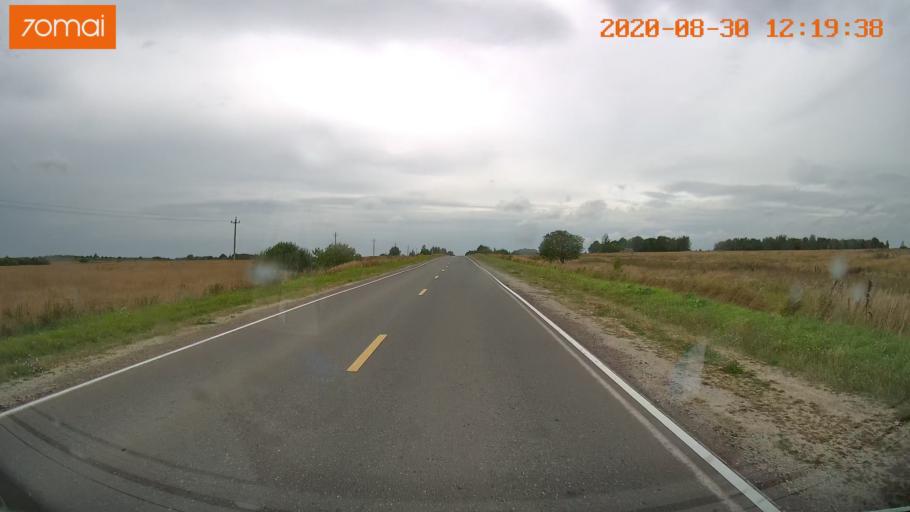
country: RU
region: Ivanovo
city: Yur'yevets
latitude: 57.3230
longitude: 42.9222
